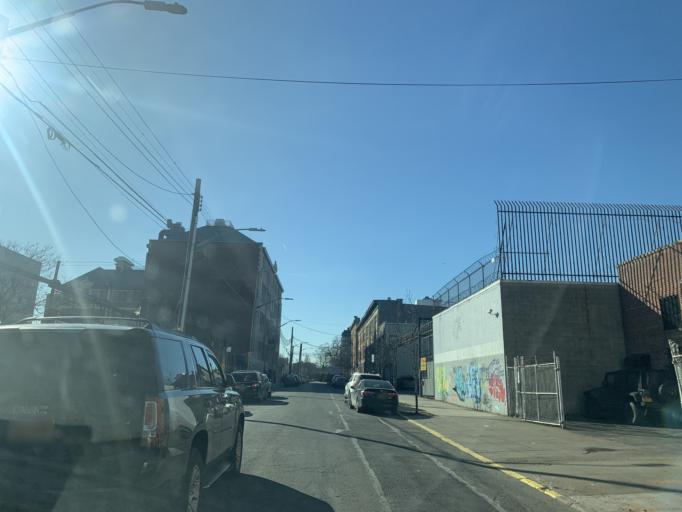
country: US
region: New York
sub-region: Queens County
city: Long Island City
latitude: 40.7052
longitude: -73.9219
